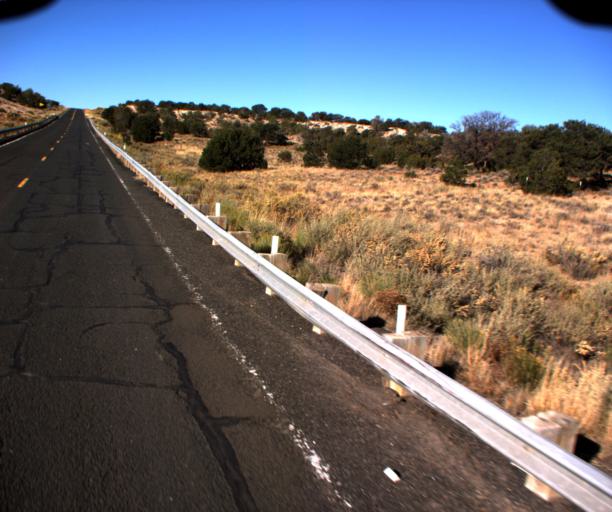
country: US
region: Arizona
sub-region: Navajo County
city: First Mesa
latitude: 35.7663
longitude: -109.9899
